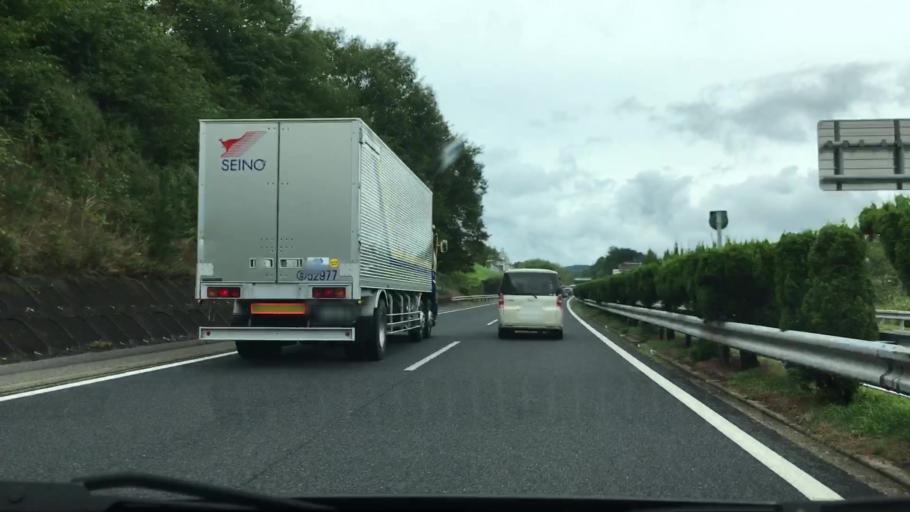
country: JP
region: Okayama
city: Tsuyama
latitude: 35.0280
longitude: 134.1585
